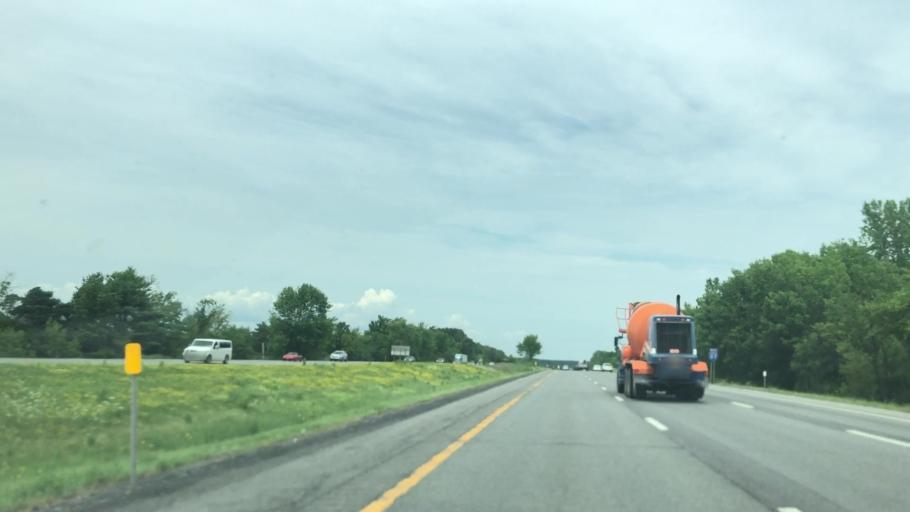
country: US
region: New York
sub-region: Saratoga County
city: Ballston Spa
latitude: 42.9777
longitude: -73.8023
